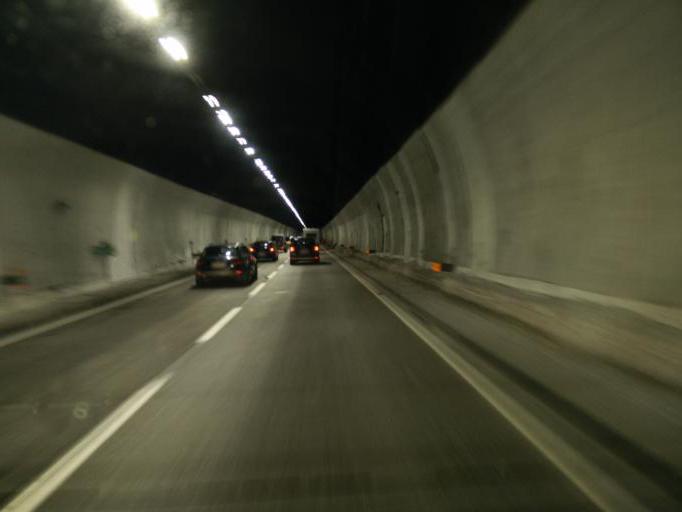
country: IT
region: Tuscany
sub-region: Province of Florence
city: Cavallina
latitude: 43.9415
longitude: 11.2207
